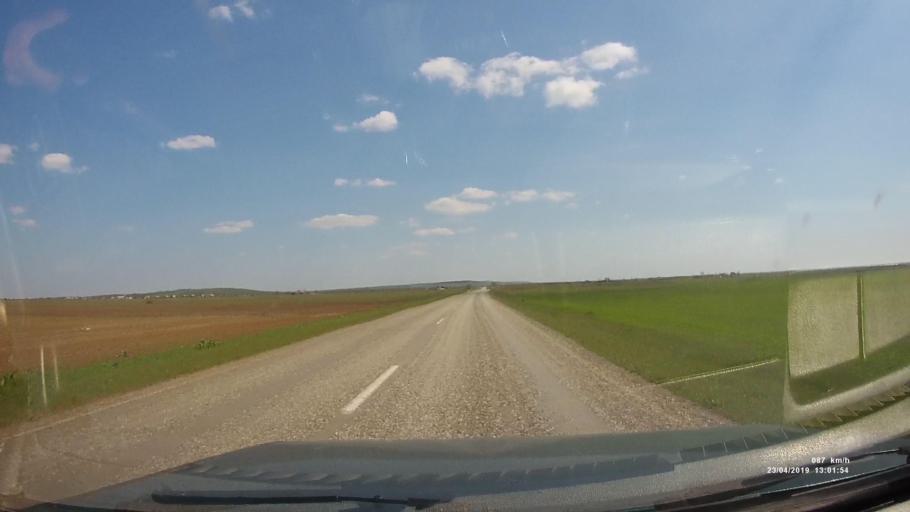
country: RU
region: Kalmykiya
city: Yashalta
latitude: 46.6028
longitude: 42.6609
